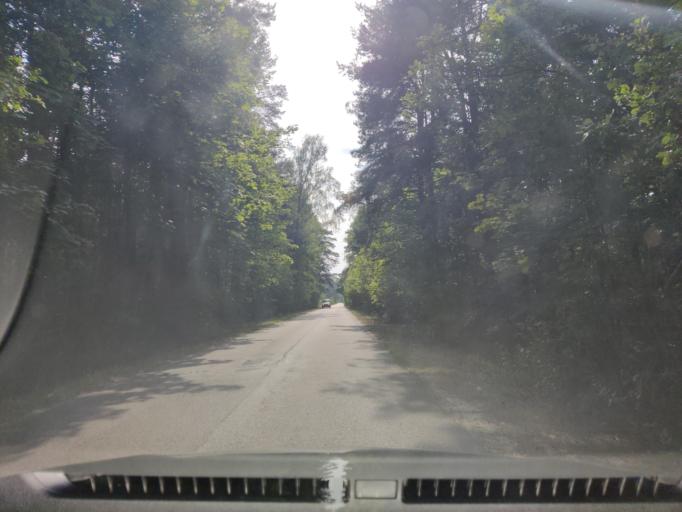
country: PL
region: Masovian Voivodeship
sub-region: Powiat wyszkowski
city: Rzasnik
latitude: 52.7725
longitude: 21.4090
